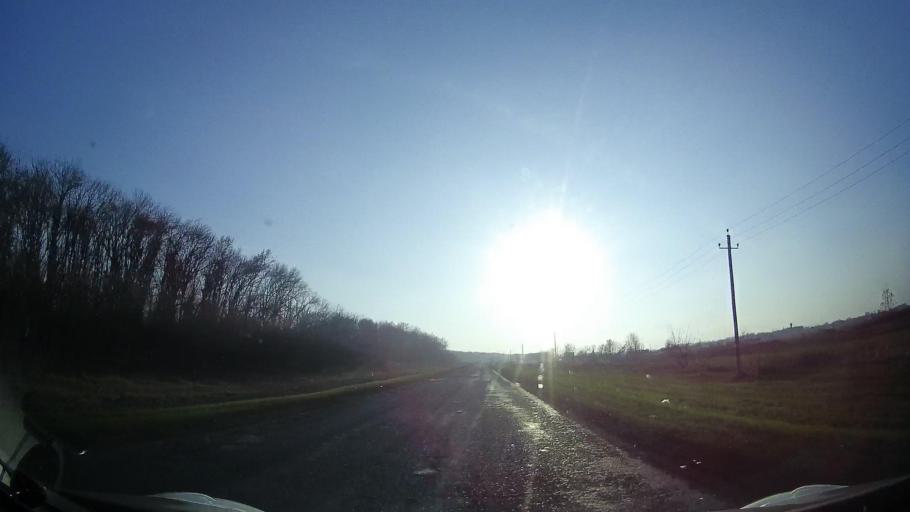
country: RU
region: Rostov
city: Ol'ginskaya
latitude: 47.1409
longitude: 39.8999
